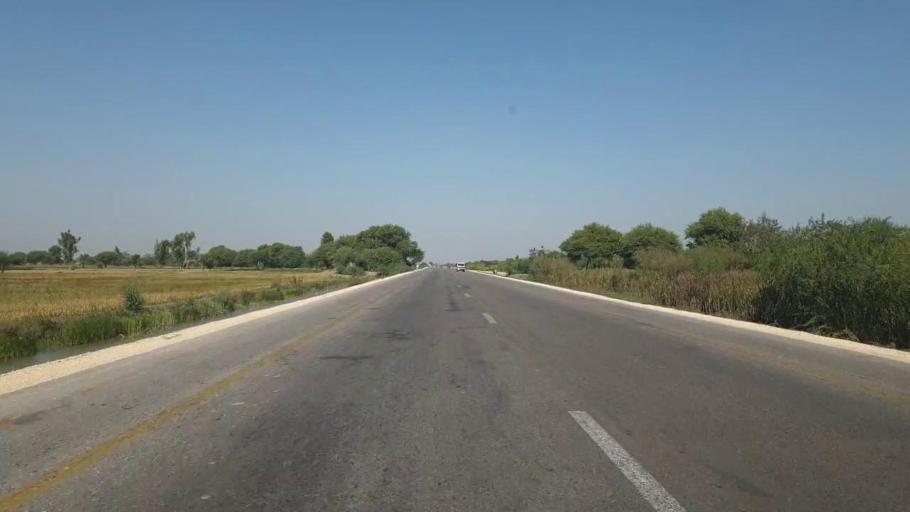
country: PK
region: Sindh
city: Talhar
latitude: 24.8195
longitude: 68.8158
